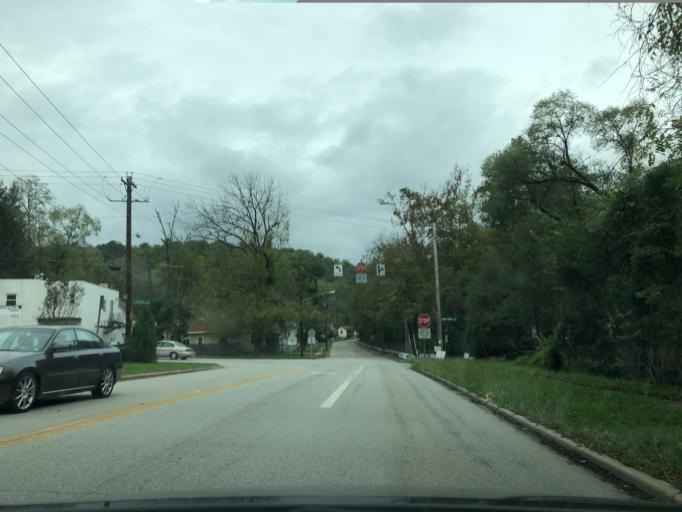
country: US
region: Ohio
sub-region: Hamilton County
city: Mariemont
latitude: 39.1593
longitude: -84.3814
